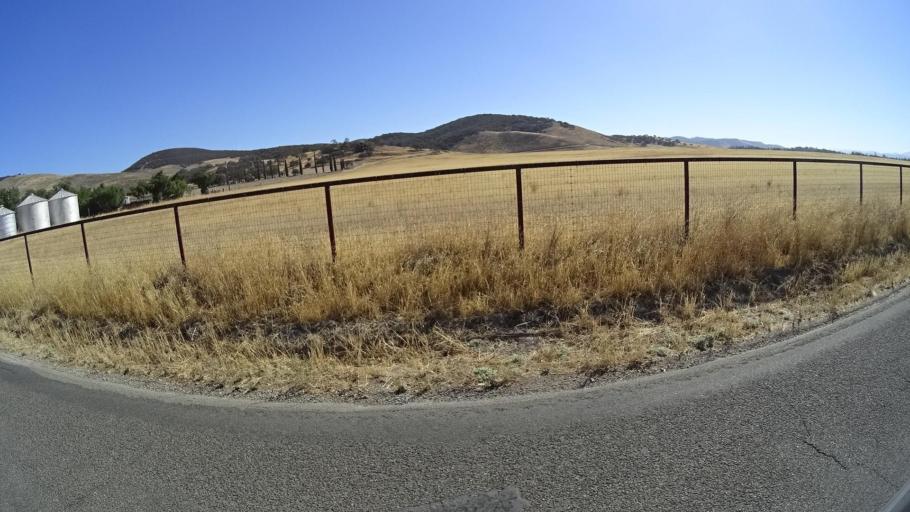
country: US
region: California
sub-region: Monterey County
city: King City
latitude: 35.9656
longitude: -121.0820
